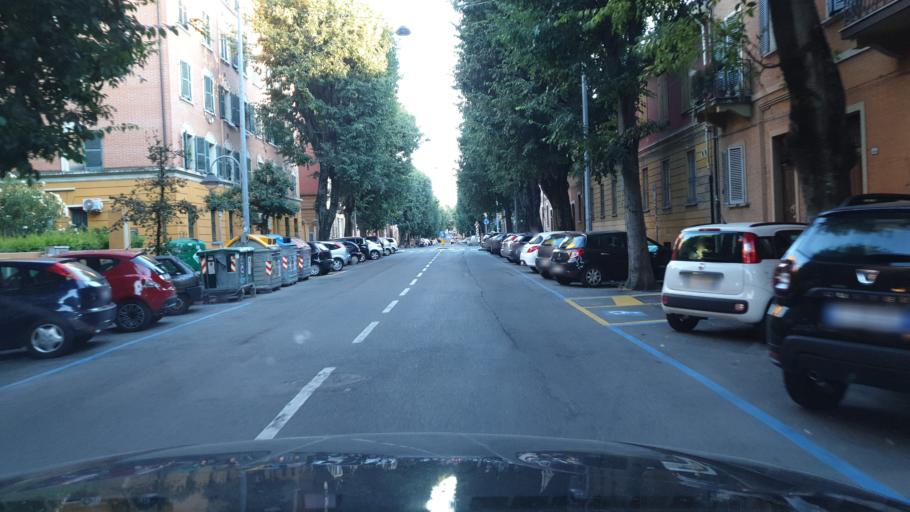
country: IT
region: Emilia-Romagna
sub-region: Provincia di Bologna
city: Bologna
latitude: 44.4960
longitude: 11.3625
